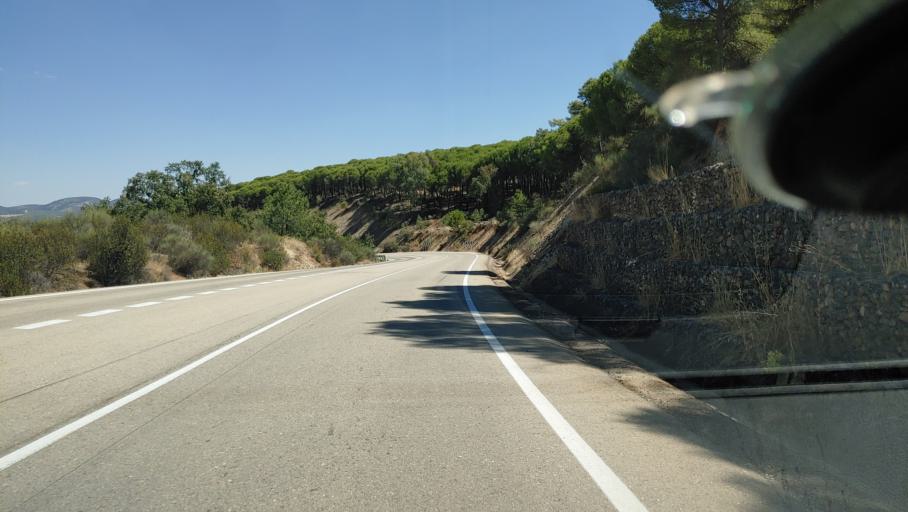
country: ES
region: Castille-La Mancha
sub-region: Provincia de Ciudad Real
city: Saceruela
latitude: 39.0074
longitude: -4.5098
